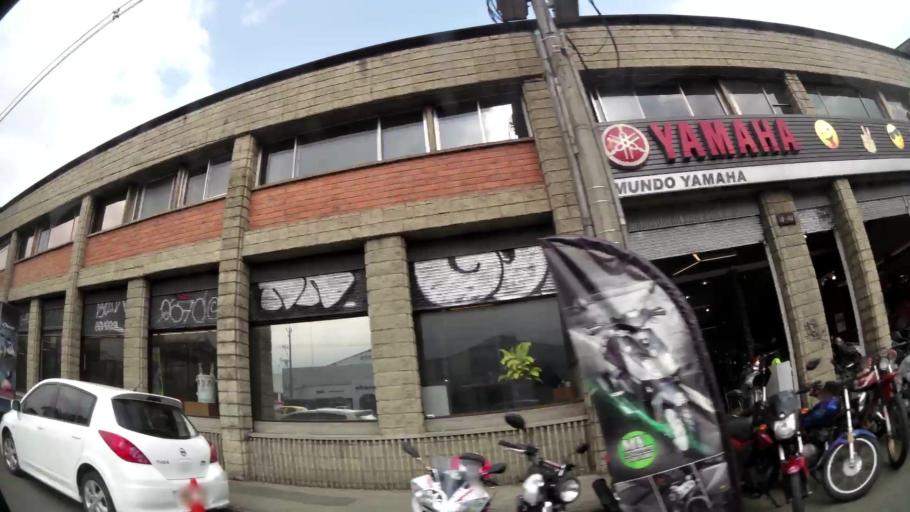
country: CO
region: Antioquia
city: Itagui
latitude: 6.2166
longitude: -75.5812
